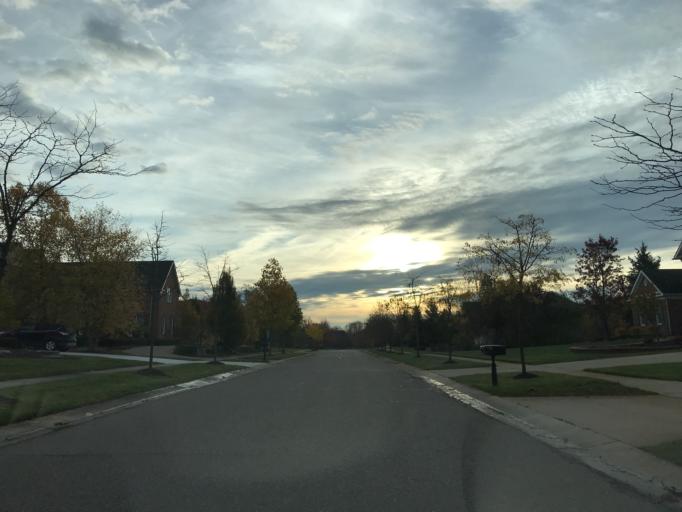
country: US
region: Michigan
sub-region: Oakland County
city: Wixom
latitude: 42.4781
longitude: -83.5436
